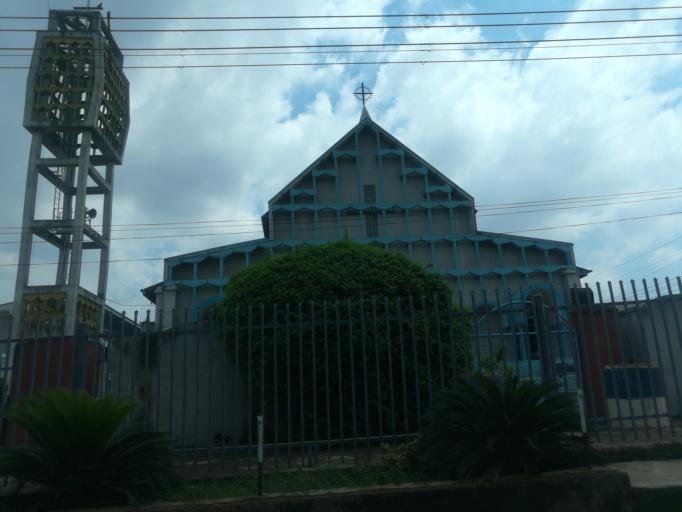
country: NG
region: Oyo
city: Ibadan
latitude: 7.3872
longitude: 3.8862
